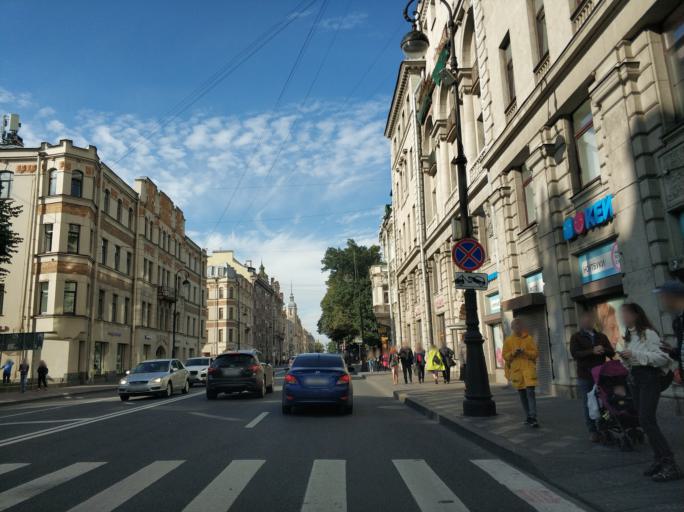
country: RU
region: St.-Petersburg
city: Petrogradka
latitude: 59.9582
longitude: 30.3191
